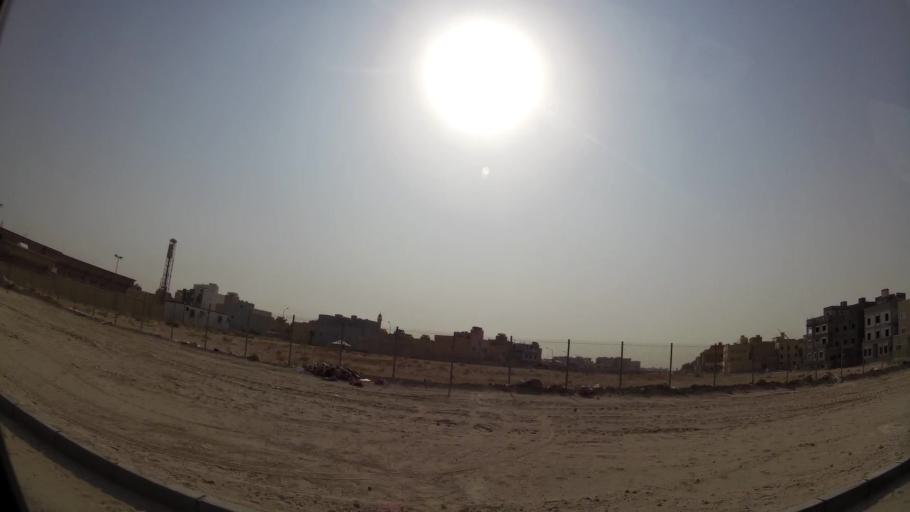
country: KW
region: Muhafazat al Jahra'
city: Al Jahra'
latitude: 29.3590
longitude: 47.7489
